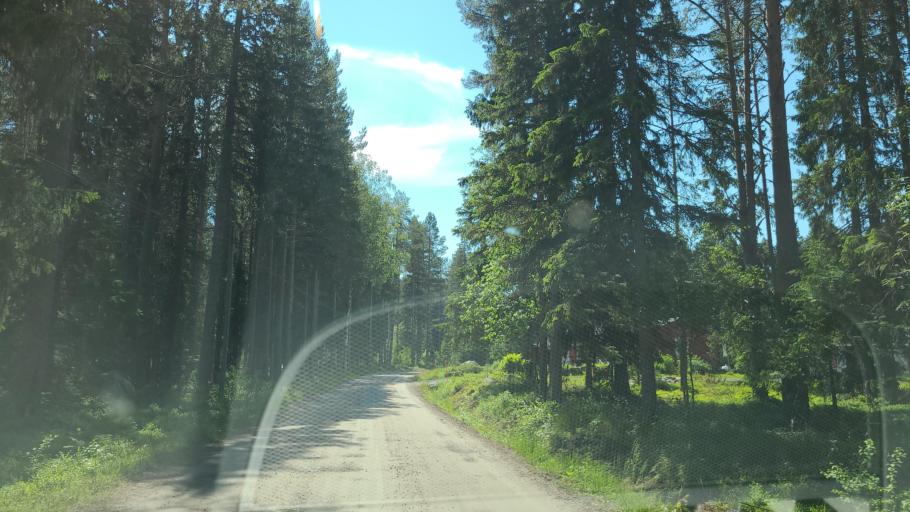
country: SE
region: Vaesterbotten
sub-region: Robertsfors Kommun
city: Robertsfors
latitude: 64.1440
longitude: 20.9608
